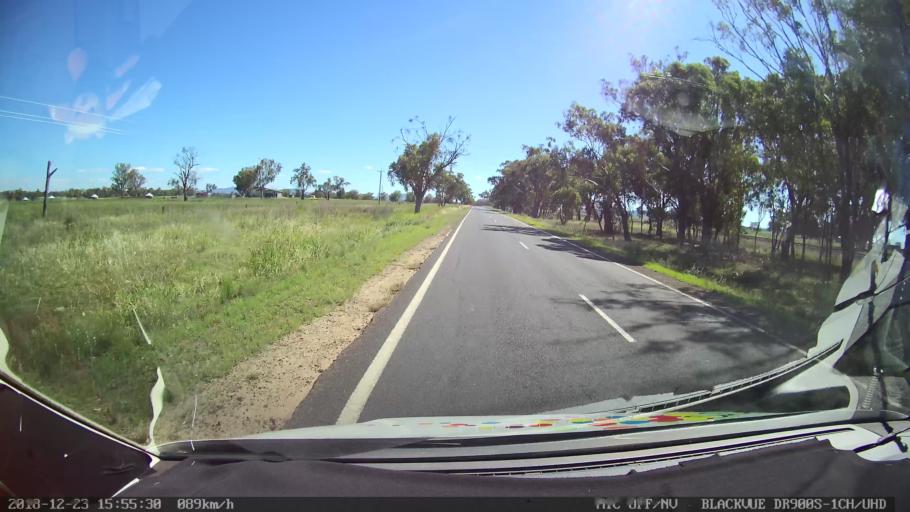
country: AU
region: New South Wales
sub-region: Tamworth Municipality
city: Phillip
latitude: -31.1561
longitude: 150.8678
